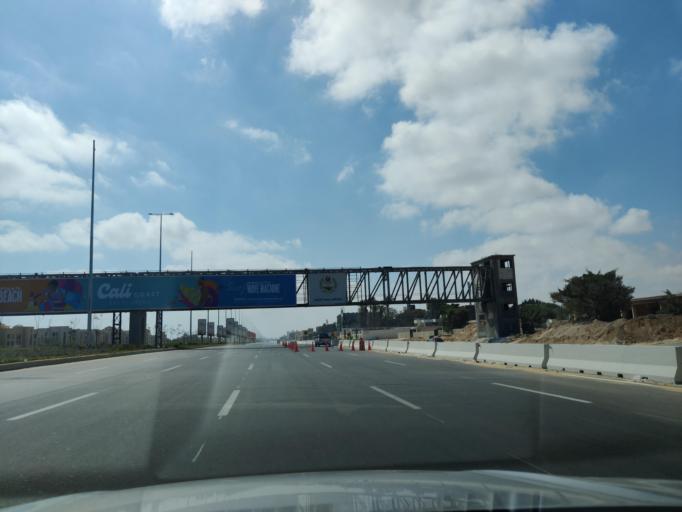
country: EG
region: Muhafazat Matruh
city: Al `Alamayn
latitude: 30.9691
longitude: 28.7422
